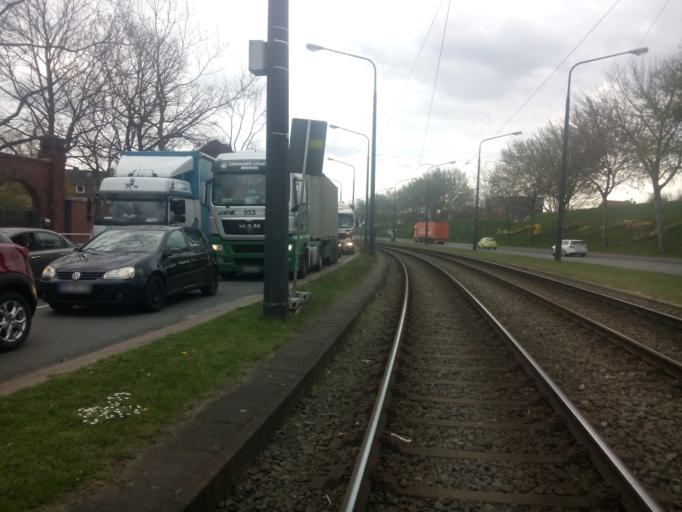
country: DE
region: Bremen
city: Bremen
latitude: 53.0967
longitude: 8.7769
